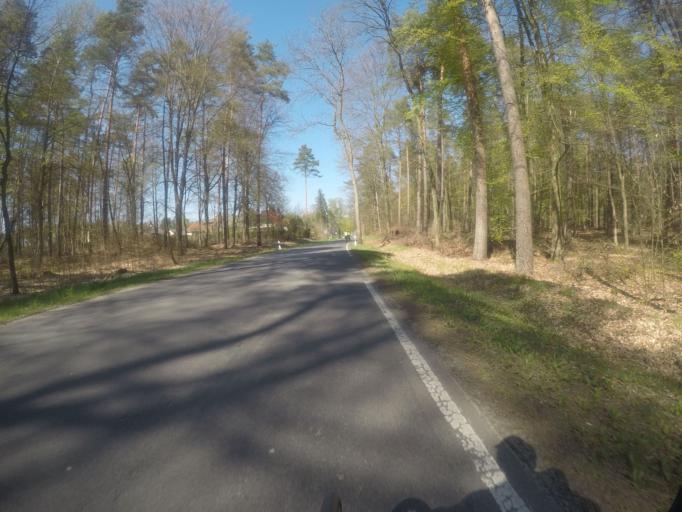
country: DE
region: Brandenburg
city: Rudnitz
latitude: 52.7522
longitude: 13.5662
